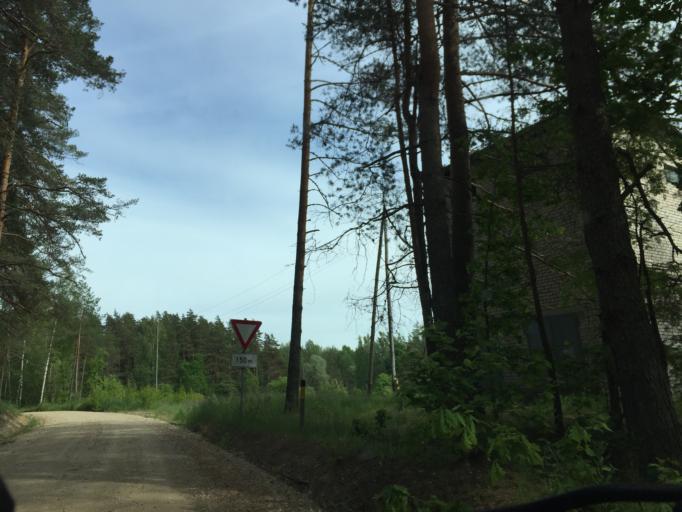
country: LV
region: Valmieras Rajons
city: Valmiera
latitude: 57.4725
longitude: 25.4015
